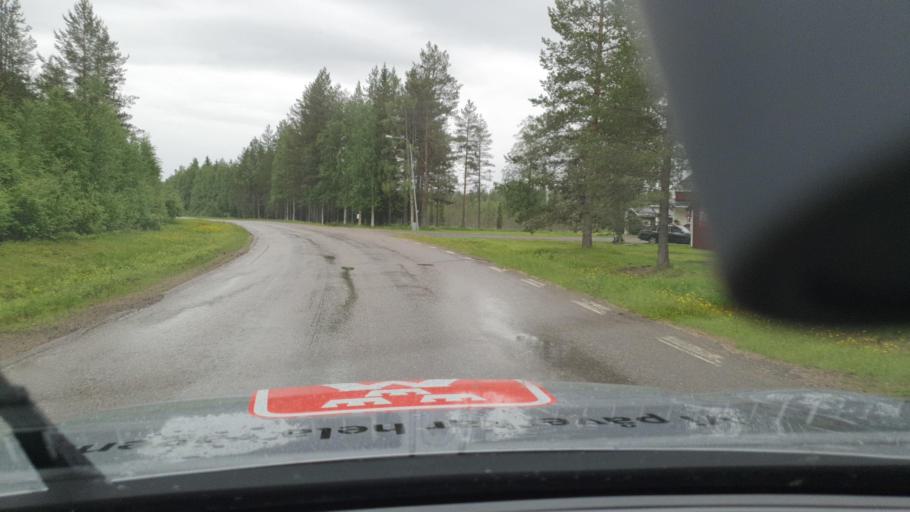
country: SE
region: Norrbotten
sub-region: Pajala Kommun
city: Pajala
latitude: 66.8204
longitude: 23.1162
